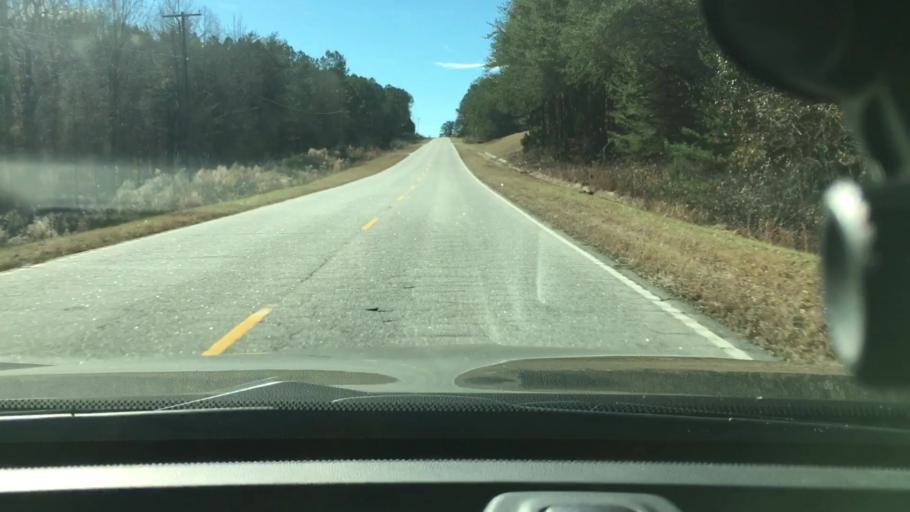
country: US
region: South Carolina
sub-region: Spartanburg County
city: Pacolet
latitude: 34.9581
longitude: -81.7106
